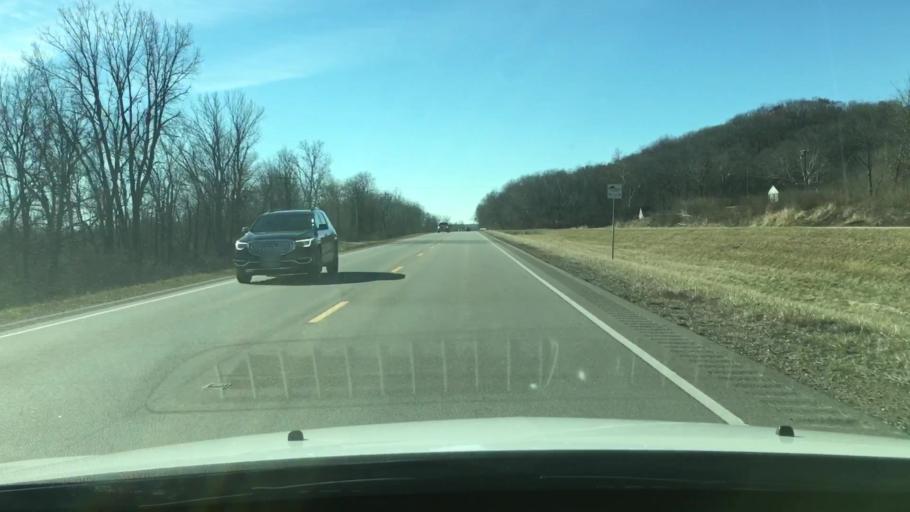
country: US
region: Illinois
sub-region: Peoria County
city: Glasford
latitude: 40.5315
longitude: -89.8731
